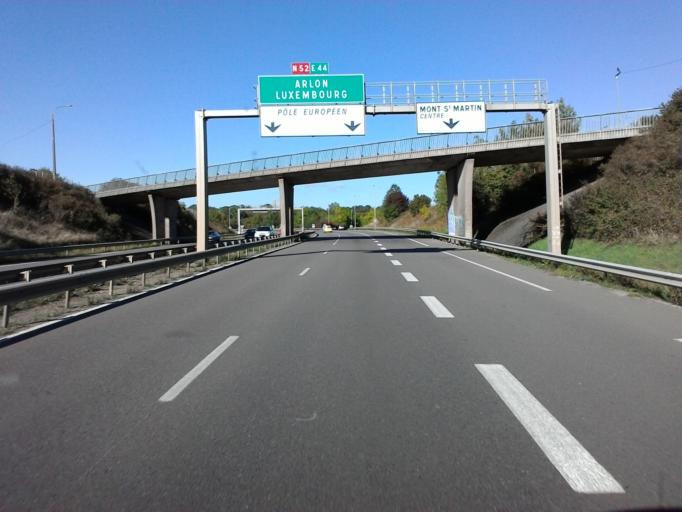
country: FR
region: Lorraine
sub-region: Departement de Meurthe-et-Moselle
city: Longwy
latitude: 49.5305
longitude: 5.7566
